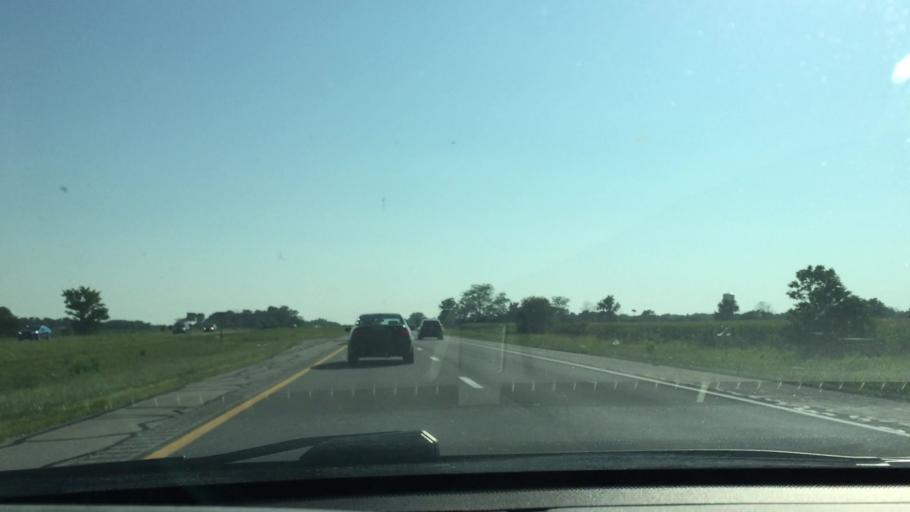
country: US
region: Ohio
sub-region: Madison County
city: Bethel
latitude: 39.7018
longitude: -83.4450
